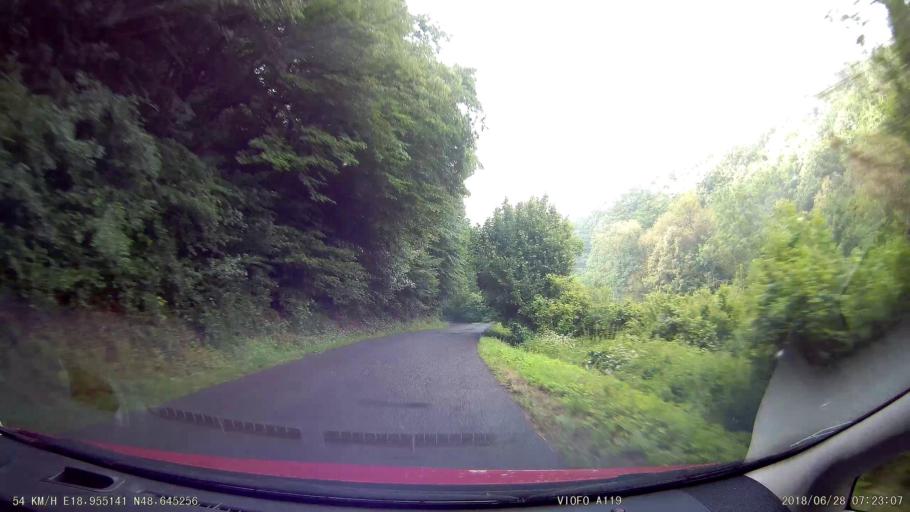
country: SK
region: Banskobystricky
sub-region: Okres Ziar nad Hronom
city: Kremnica
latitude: 48.6450
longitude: 18.9553
